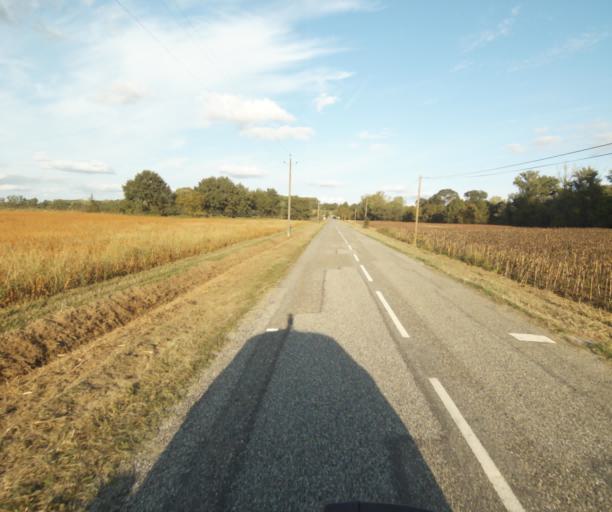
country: FR
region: Midi-Pyrenees
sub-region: Departement de la Haute-Garonne
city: Launac
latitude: 43.8178
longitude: 1.1279
